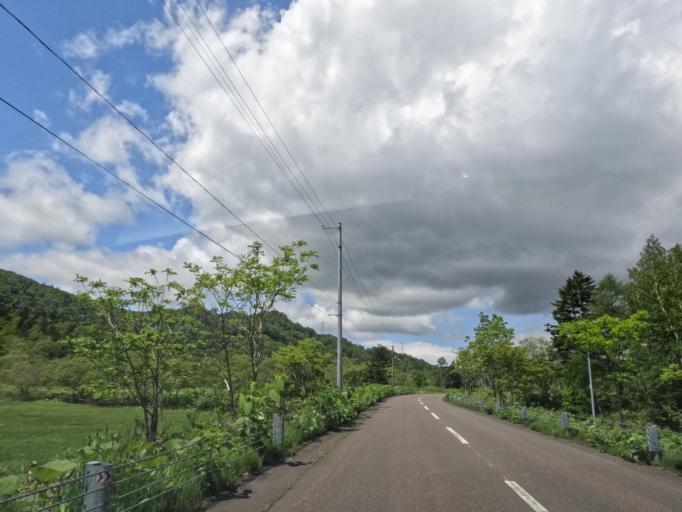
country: JP
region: Hokkaido
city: Tobetsu
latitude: 43.4383
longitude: 141.5823
